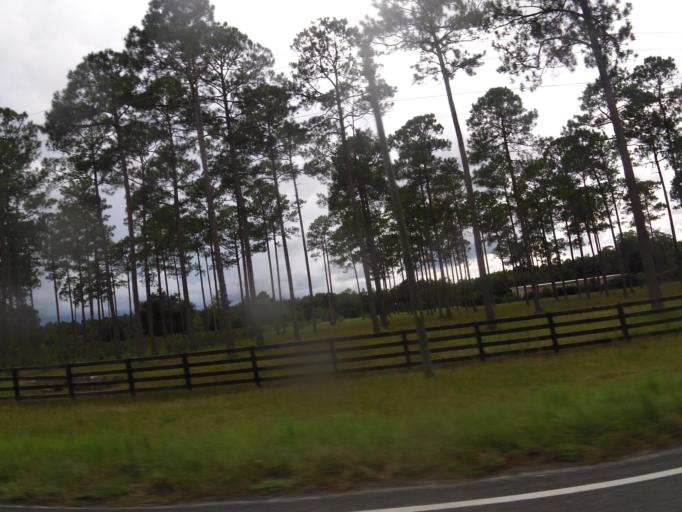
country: US
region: Florida
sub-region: Baker County
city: Macclenny
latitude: 30.4878
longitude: -82.1984
